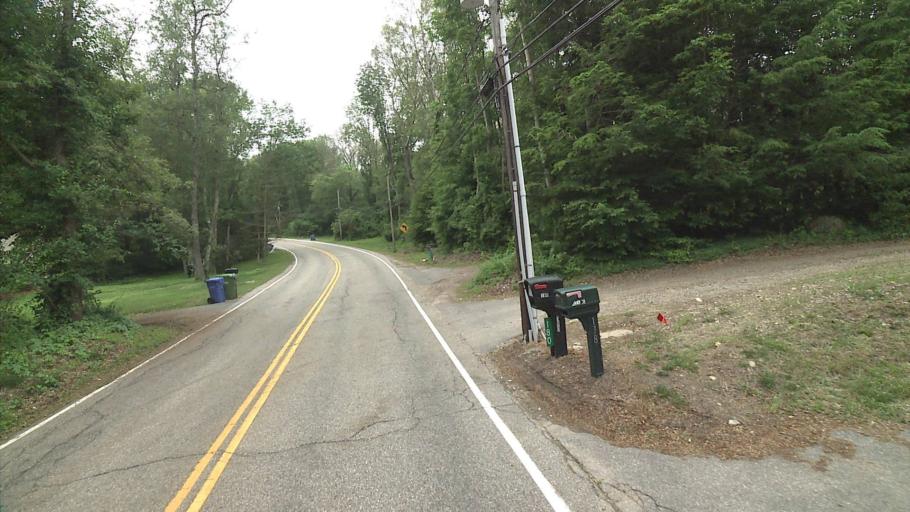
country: US
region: Connecticut
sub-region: Tolland County
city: Coventry Lake
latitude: 41.7227
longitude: -72.3712
